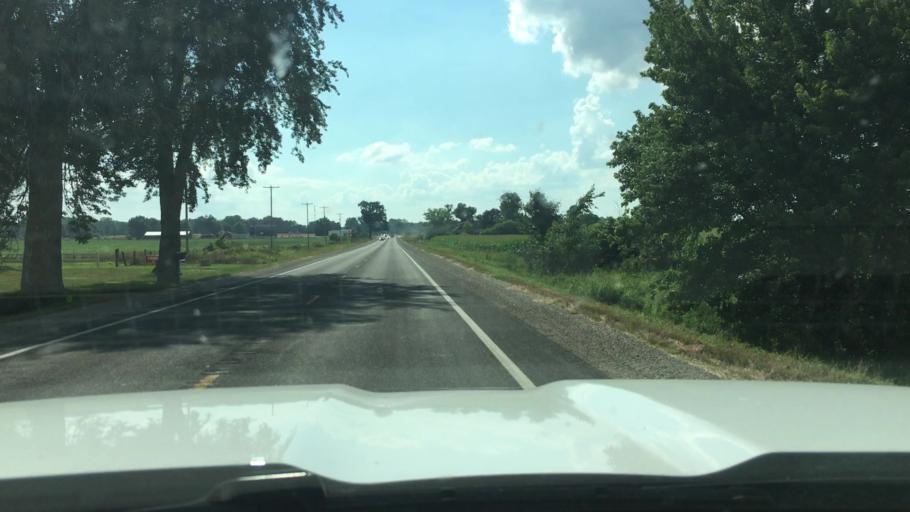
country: US
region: Michigan
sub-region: Montcalm County
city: Stanton
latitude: 43.1783
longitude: -85.0640
